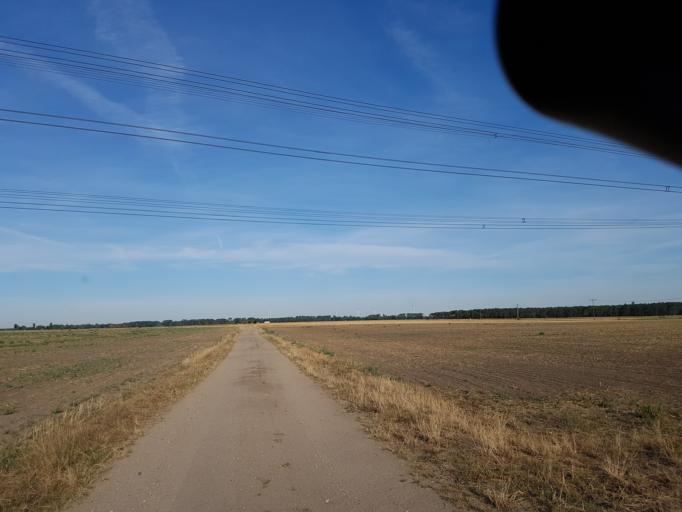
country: DE
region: Saxony
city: Nauwalde
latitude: 51.4531
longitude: 13.4099
